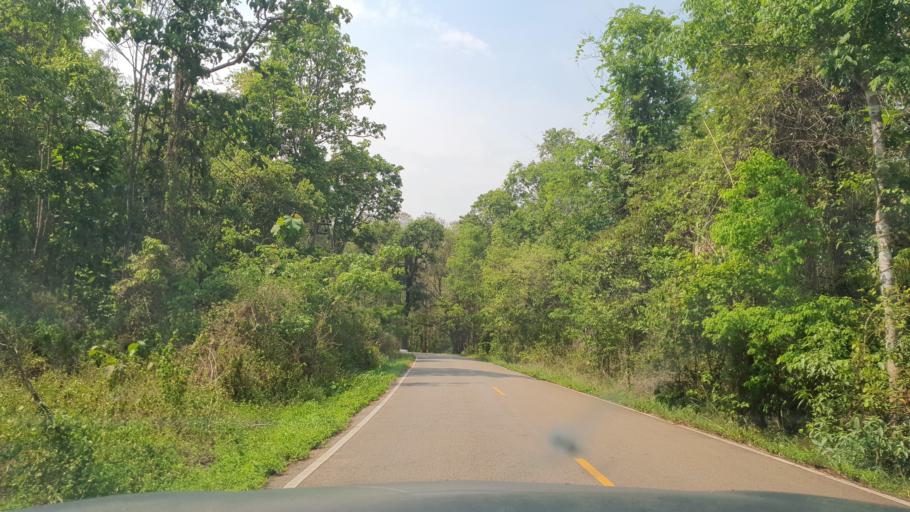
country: TH
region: Chiang Mai
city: San Sai
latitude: 19.0015
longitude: 99.1260
